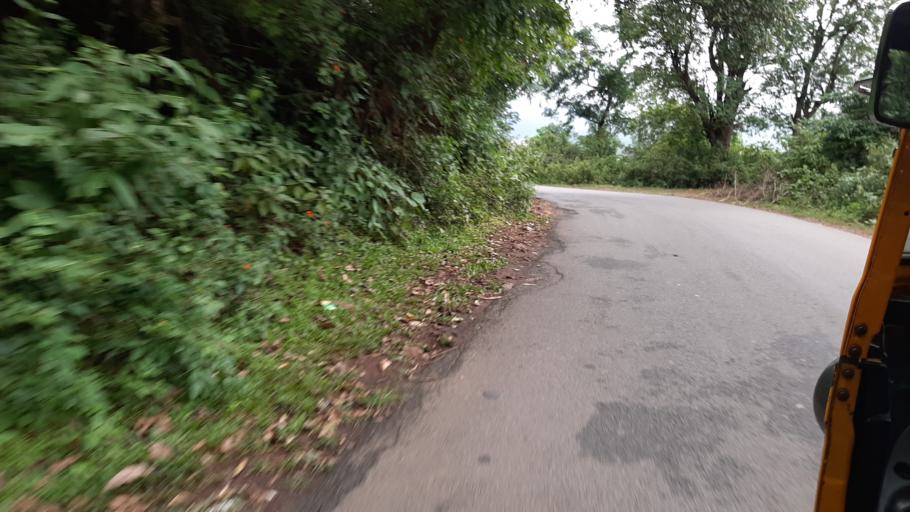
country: IN
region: Andhra Pradesh
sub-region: Vizianagaram District
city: Salur
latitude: 18.2461
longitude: 83.0245
